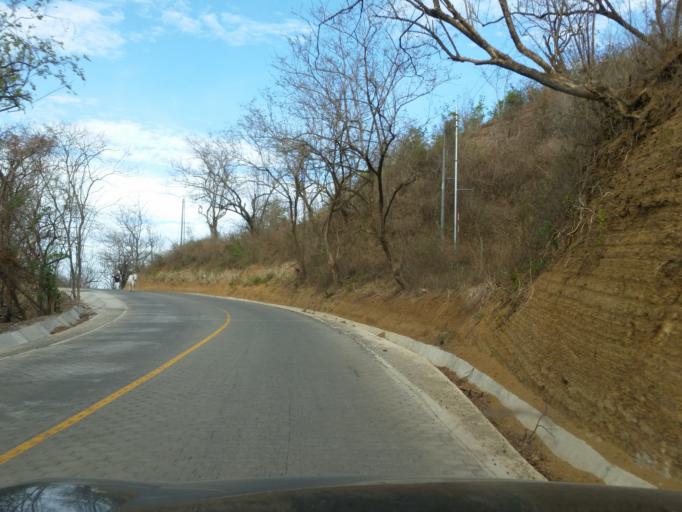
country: NI
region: Rivas
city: Tola
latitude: 11.3910
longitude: -85.9856
